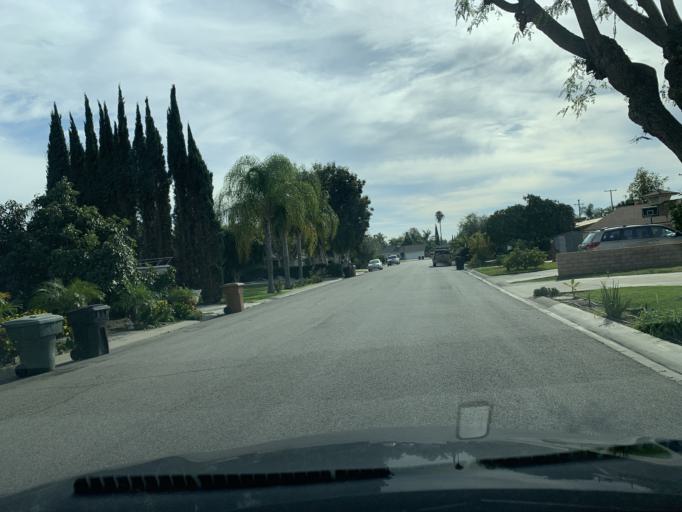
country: US
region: California
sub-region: Orange County
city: Garden Grove
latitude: 33.7869
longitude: -117.9354
